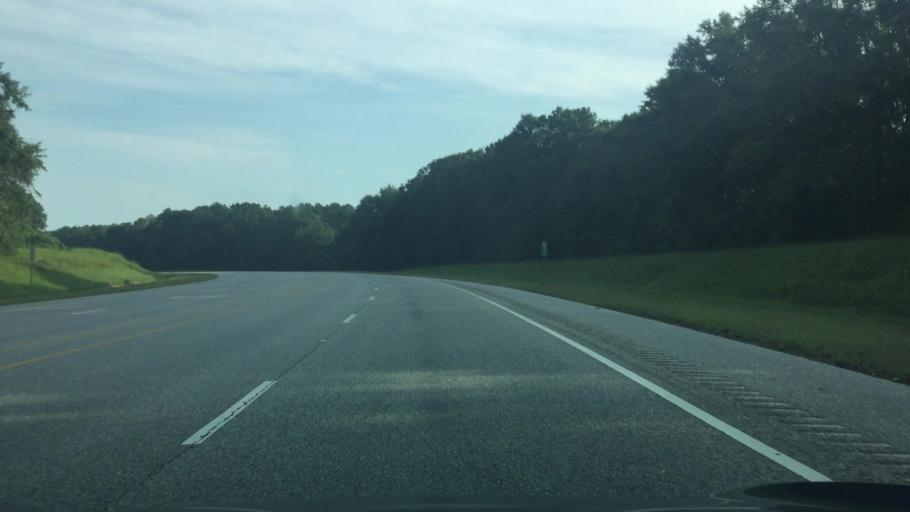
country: US
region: Alabama
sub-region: Butler County
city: Georgiana
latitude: 31.5106
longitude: -86.7014
